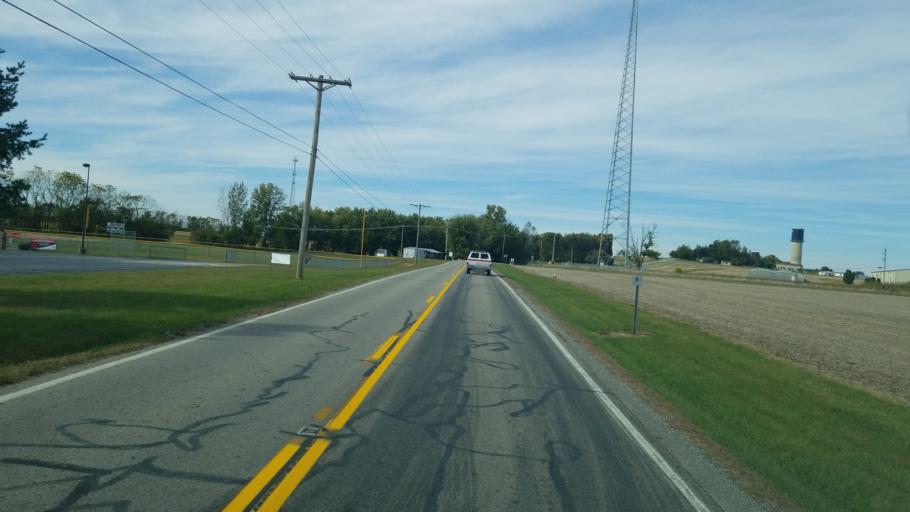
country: US
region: Ohio
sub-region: Highland County
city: Leesburg
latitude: 39.3303
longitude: -83.5464
